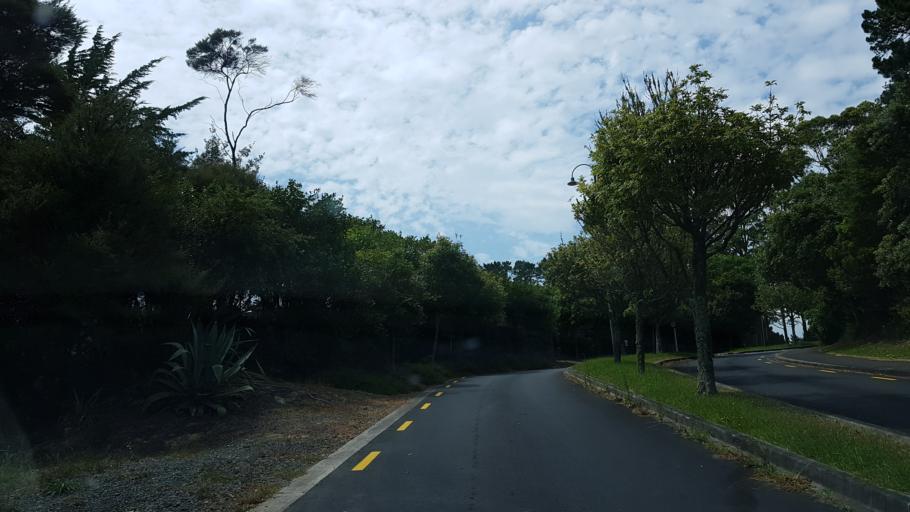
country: NZ
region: Auckland
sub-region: Auckland
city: North Shore
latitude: -36.7771
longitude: 174.6877
